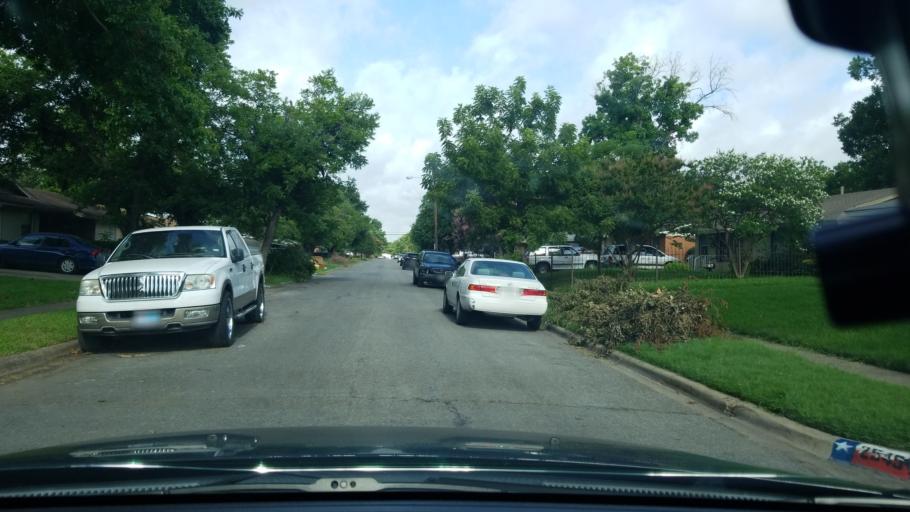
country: US
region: Texas
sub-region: Dallas County
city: Mesquite
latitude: 32.8152
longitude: -96.6713
